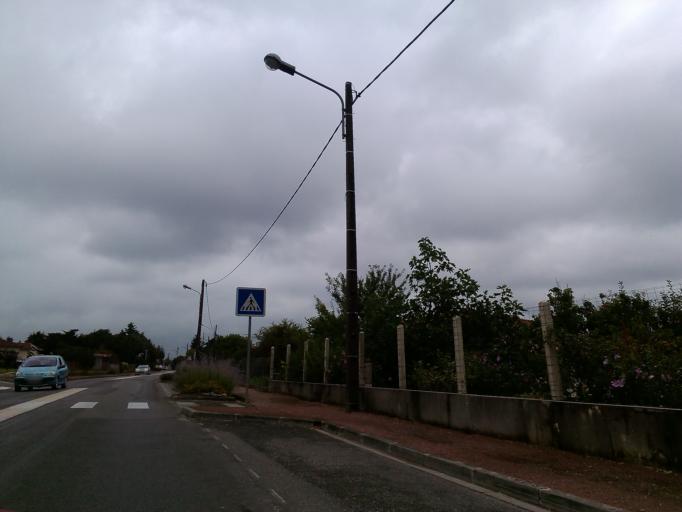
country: FR
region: Poitou-Charentes
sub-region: Departement de la Charente
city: Cognac
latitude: 45.6958
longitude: -0.3459
